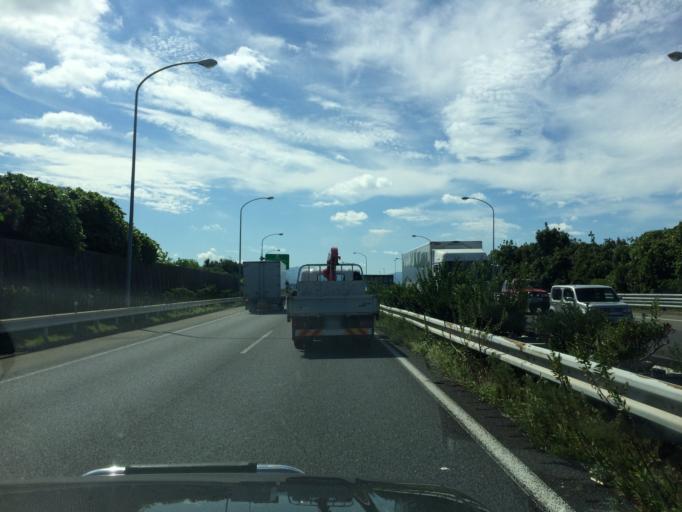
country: JP
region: Osaka
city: Takaishi
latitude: 34.5152
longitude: 135.4900
